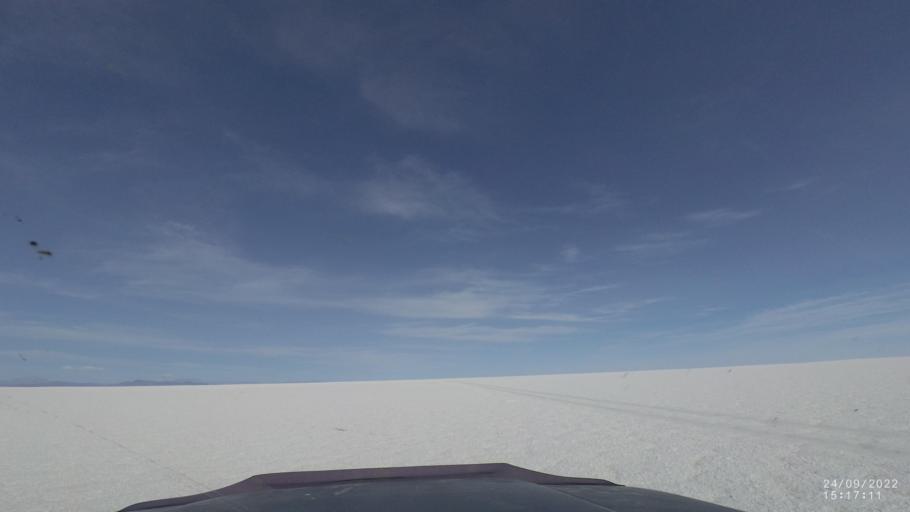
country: BO
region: Potosi
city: Colchani
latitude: -19.9874
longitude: -67.4292
